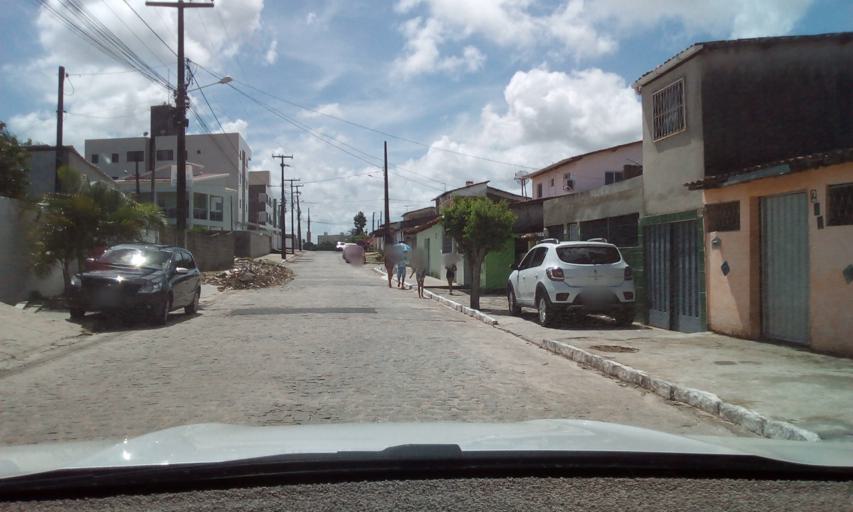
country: BR
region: Paraiba
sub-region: Joao Pessoa
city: Joao Pessoa
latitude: -7.1701
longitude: -34.8895
